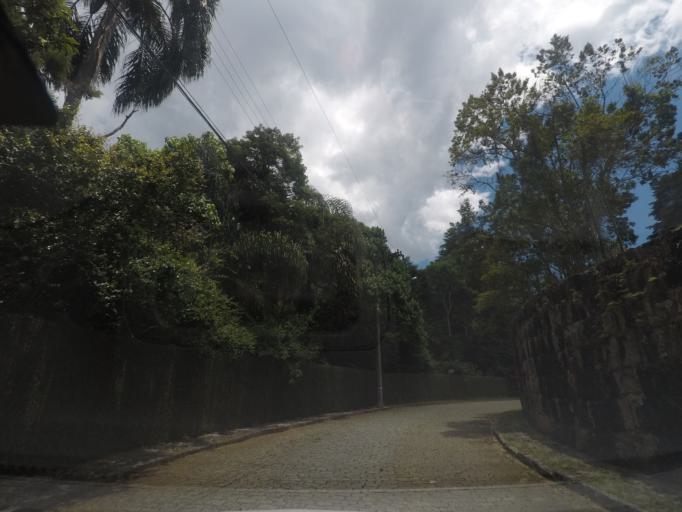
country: BR
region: Rio de Janeiro
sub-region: Petropolis
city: Petropolis
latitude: -22.5000
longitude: -43.1891
